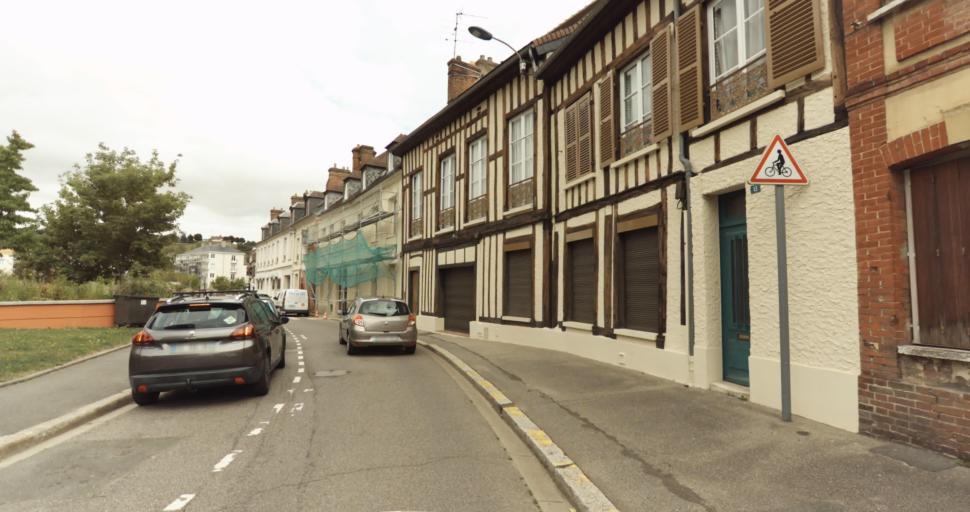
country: FR
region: Haute-Normandie
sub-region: Departement de l'Eure
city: Evreux
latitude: 49.0270
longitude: 1.1527
